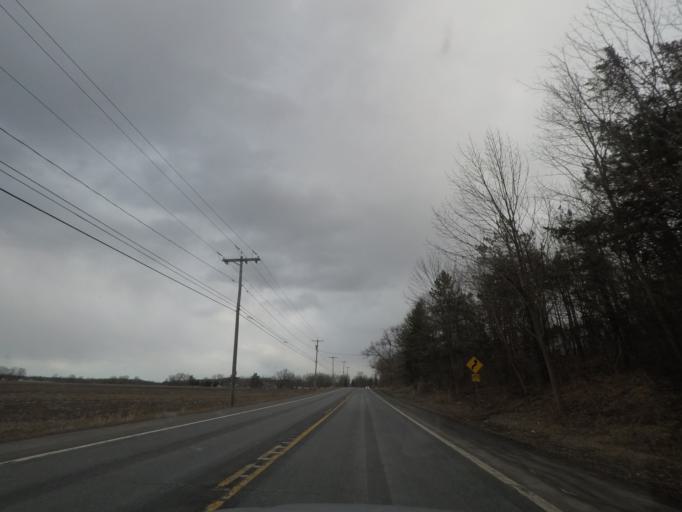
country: US
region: New York
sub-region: Madison County
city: Chittenango
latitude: 43.0544
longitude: -75.8527
